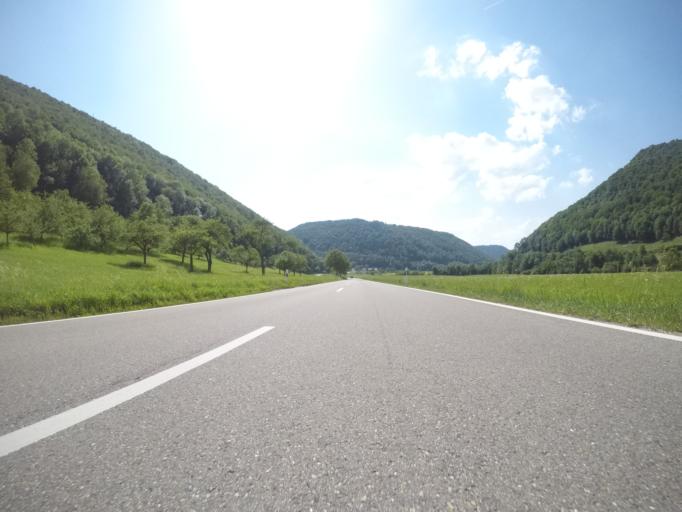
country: DE
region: Baden-Wuerttemberg
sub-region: Tuebingen Region
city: Grabenstetten
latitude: 48.5305
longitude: 9.5086
